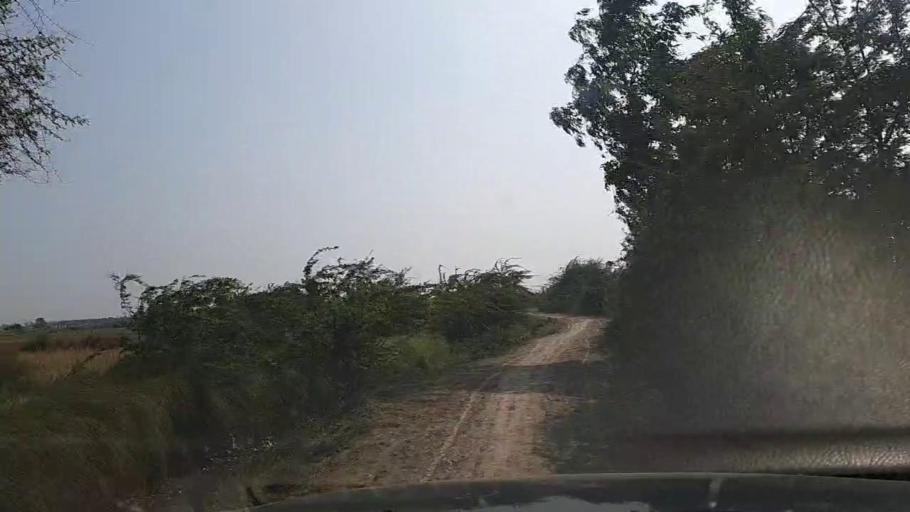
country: PK
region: Sindh
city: Gharo
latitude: 24.7375
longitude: 67.6851
